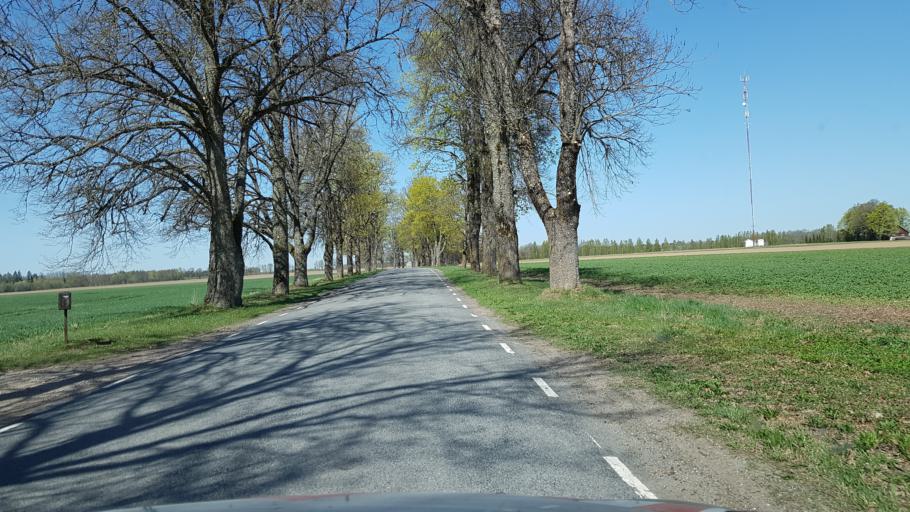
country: EE
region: Viljandimaa
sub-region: Vohma linn
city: Vohma
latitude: 58.5425
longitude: 25.5731
